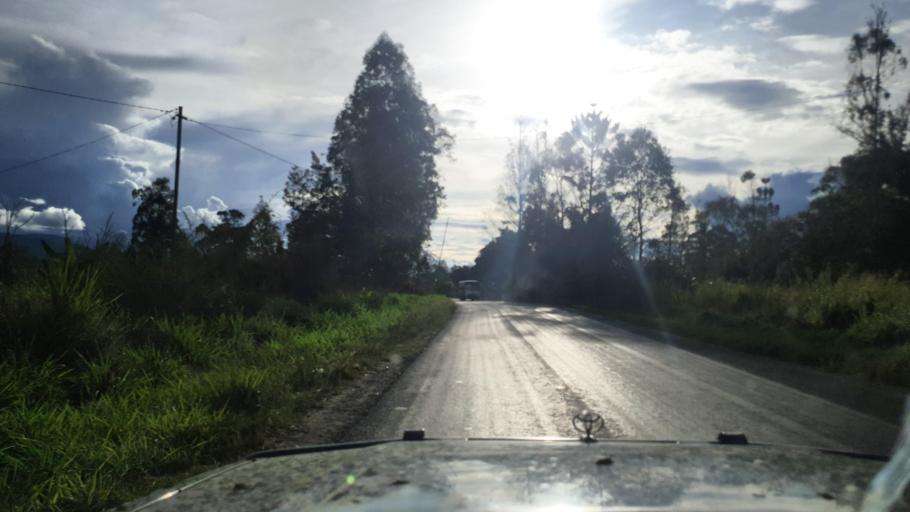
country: PG
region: Jiwaka
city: Minj
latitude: -5.8406
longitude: 144.6158
